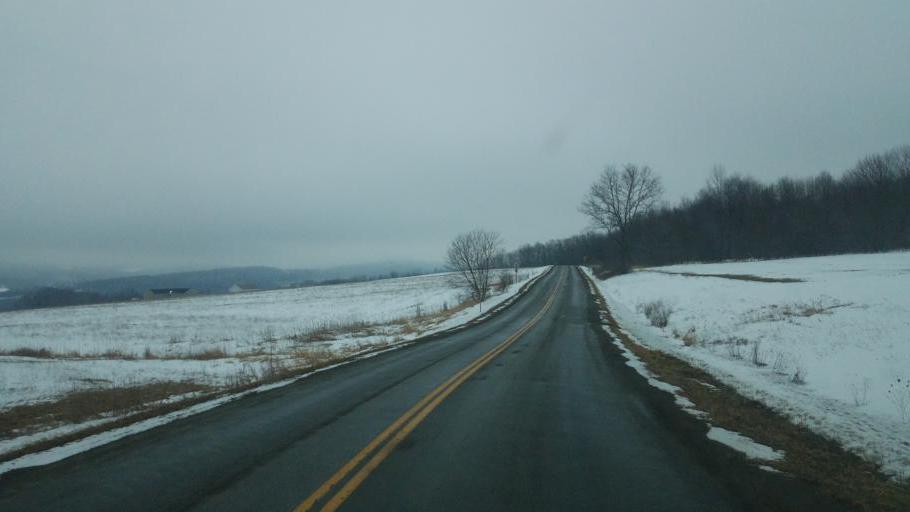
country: US
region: Pennsylvania
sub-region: Tioga County
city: Westfield
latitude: 42.0510
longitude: -77.5331
